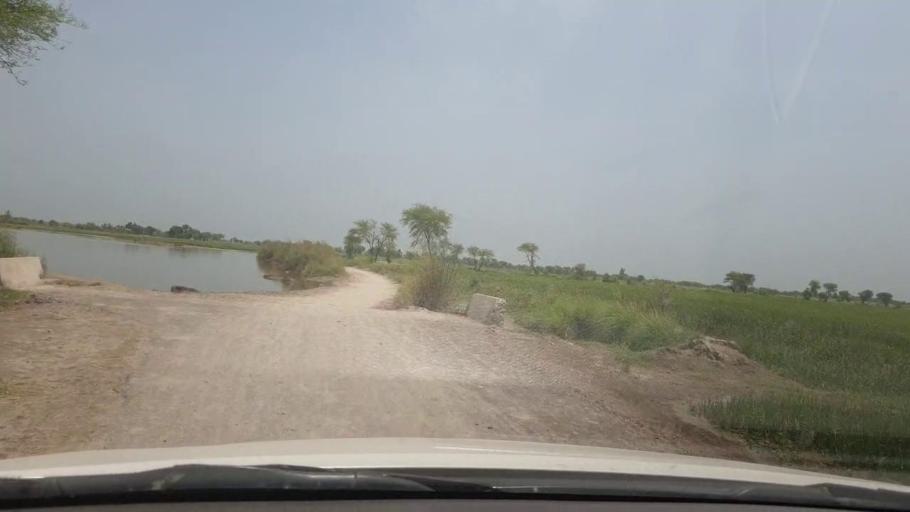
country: PK
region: Sindh
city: Shikarpur
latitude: 28.0941
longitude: 68.6308
